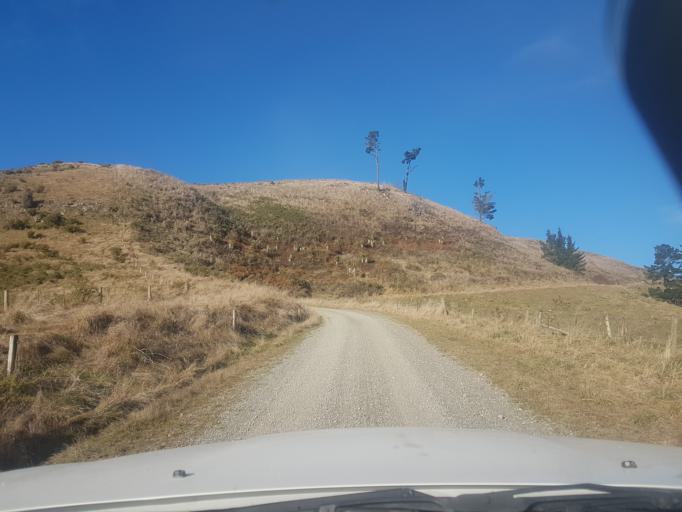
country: NZ
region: Canterbury
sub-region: Timaru District
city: Pleasant Point
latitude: -44.1663
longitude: 170.8798
